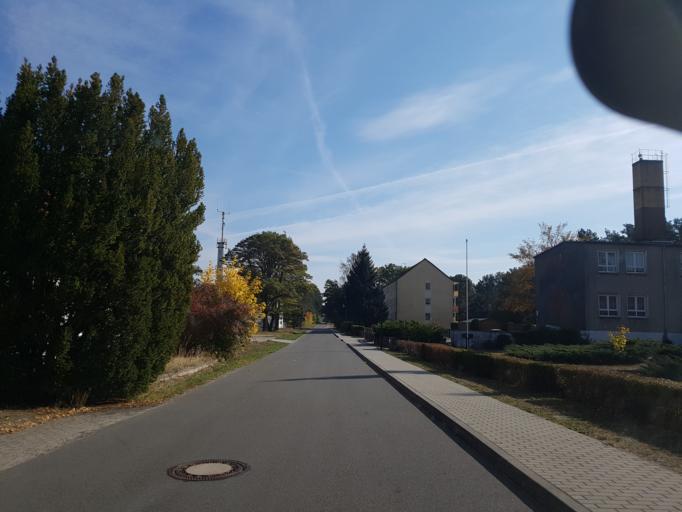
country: DE
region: Brandenburg
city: Hohenbucko
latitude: 51.7609
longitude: 13.4677
